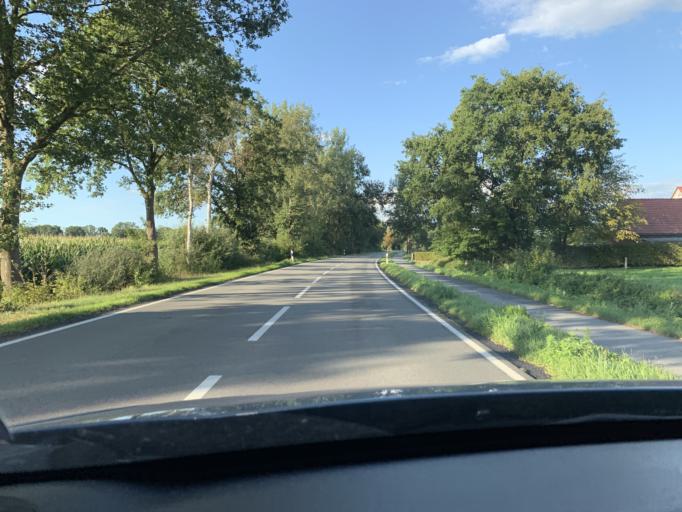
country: DE
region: Lower Saxony
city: Edewecht
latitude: 53.1056
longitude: 7.9520
